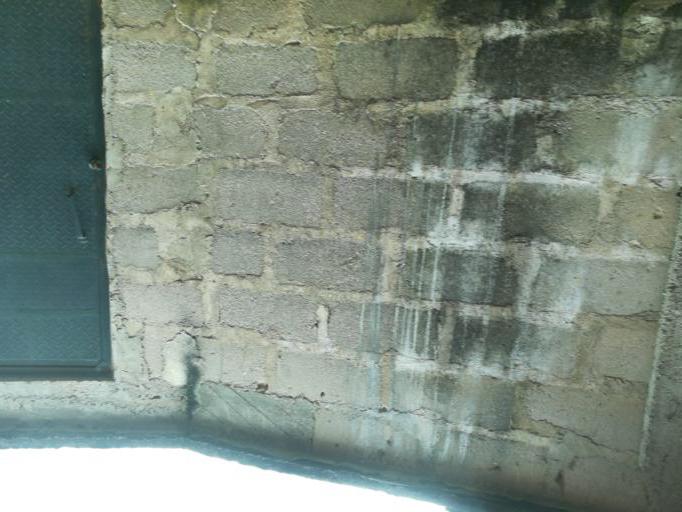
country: NG
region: Rivers
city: Emuoha
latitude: 4.9037
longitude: 6.9871
